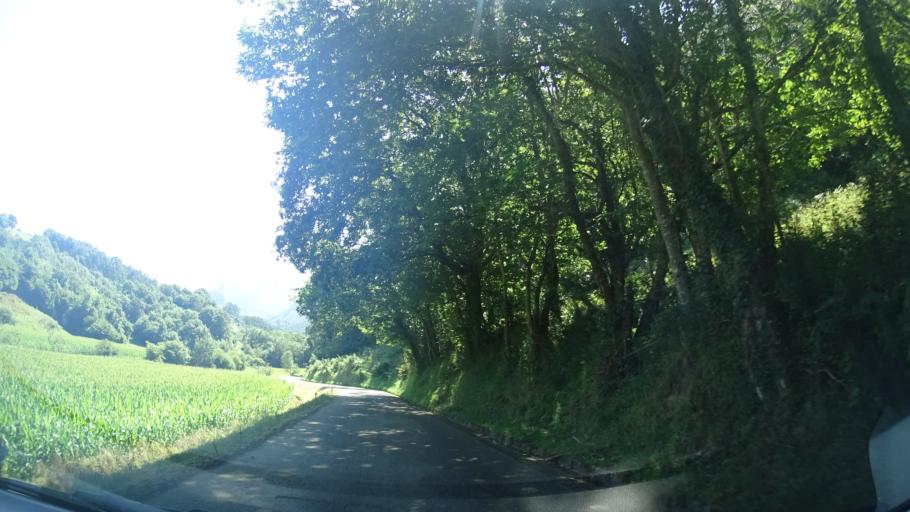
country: ES
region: Asturias
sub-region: Province of Asturias
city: Ribadesella
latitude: 43.4388
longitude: -5.0804
